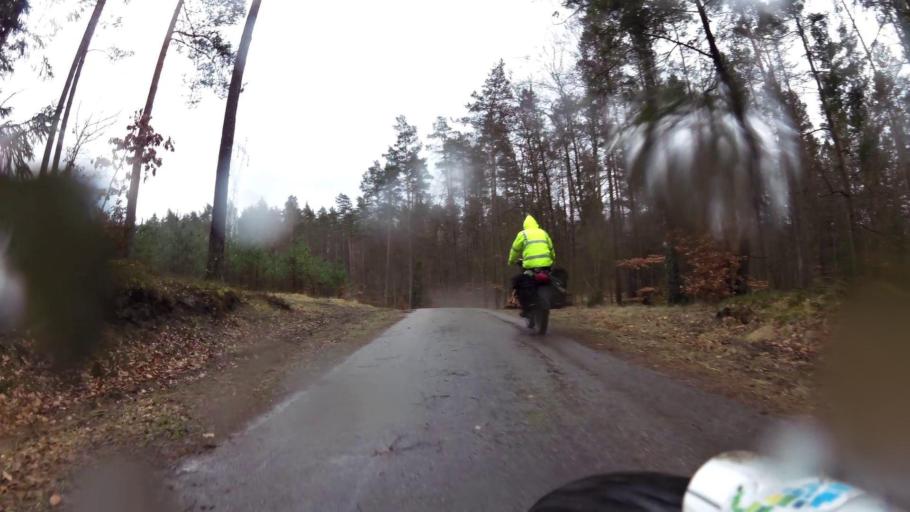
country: PL
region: Pomeranian Voivodeship
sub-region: Powiat bytowski
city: Miastko
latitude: 54.0640
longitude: 17.0768
